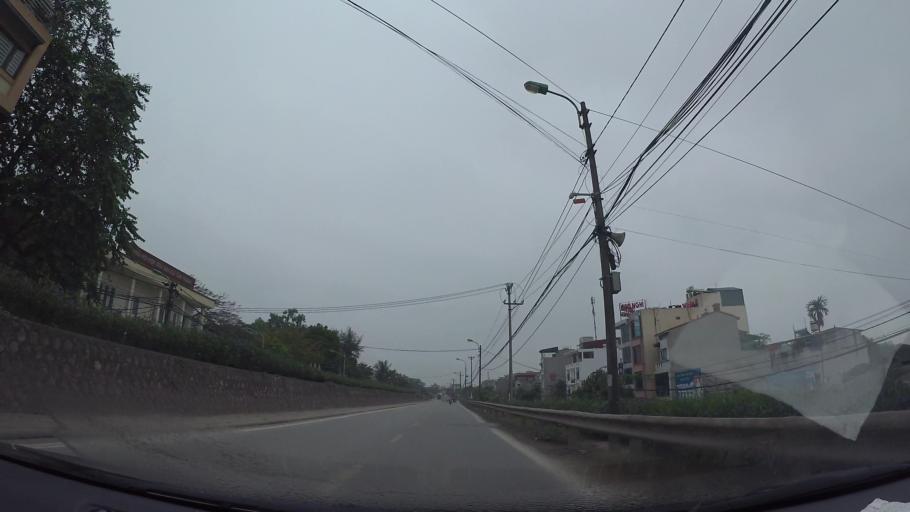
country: VN
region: Ha Noi
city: Hai BaTrung
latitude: 20.9980
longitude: 105.8889
